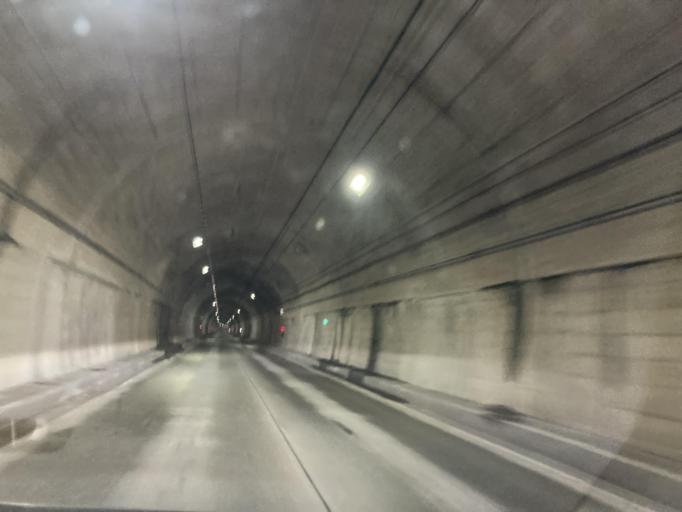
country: JP
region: Nagano
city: Omachi
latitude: 36.5035
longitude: 137.7612
